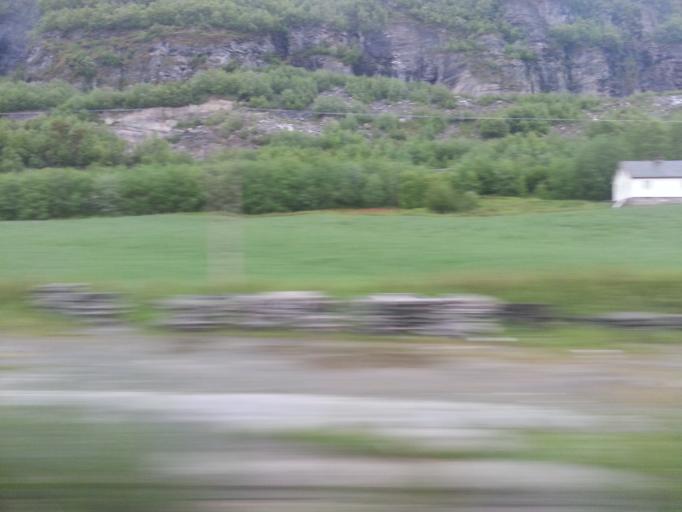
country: NO
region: Sor-Trondelag
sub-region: Oppdal
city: Oppdal
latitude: 62.4601
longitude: 9.5752
